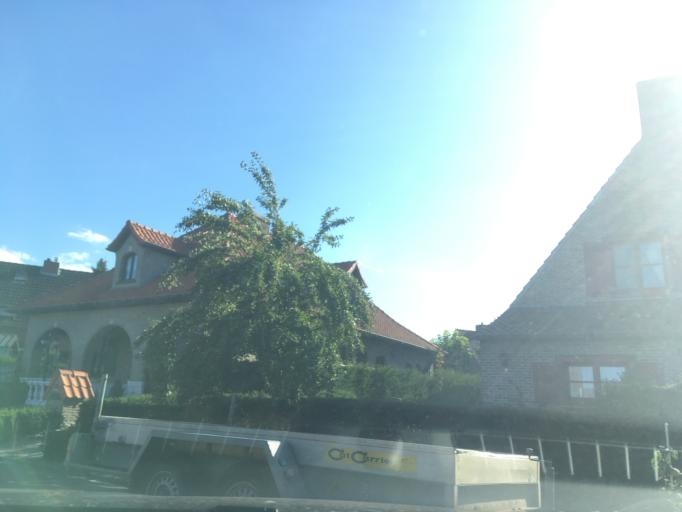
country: BE
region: Flanders
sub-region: Provincie West-Vlaanderen
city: Lichtervelde
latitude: 51.0250
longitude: 3.1507
